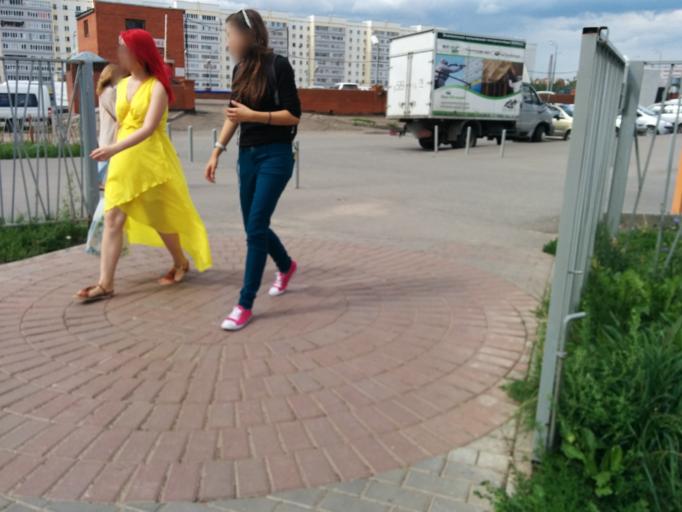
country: RU
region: Tatarstan
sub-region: Gorod Kazan'
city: Kazan
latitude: 55.7469
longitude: 49.2051
